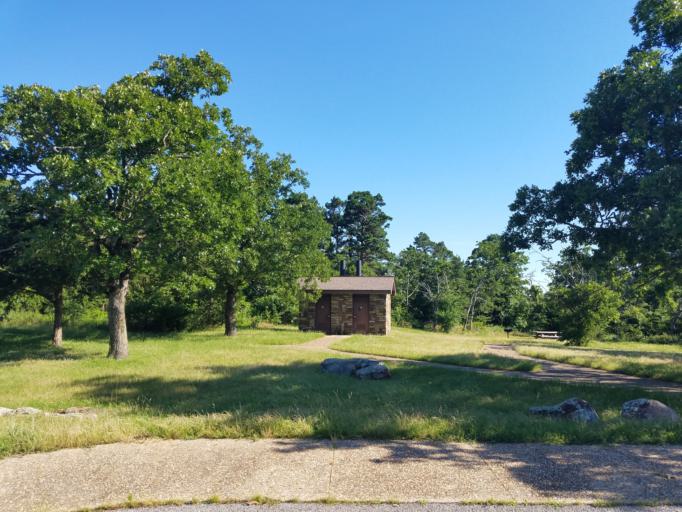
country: US
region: Oklahoma
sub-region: Le Flore County
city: Talihina
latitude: 34.7964
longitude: -94.9450
